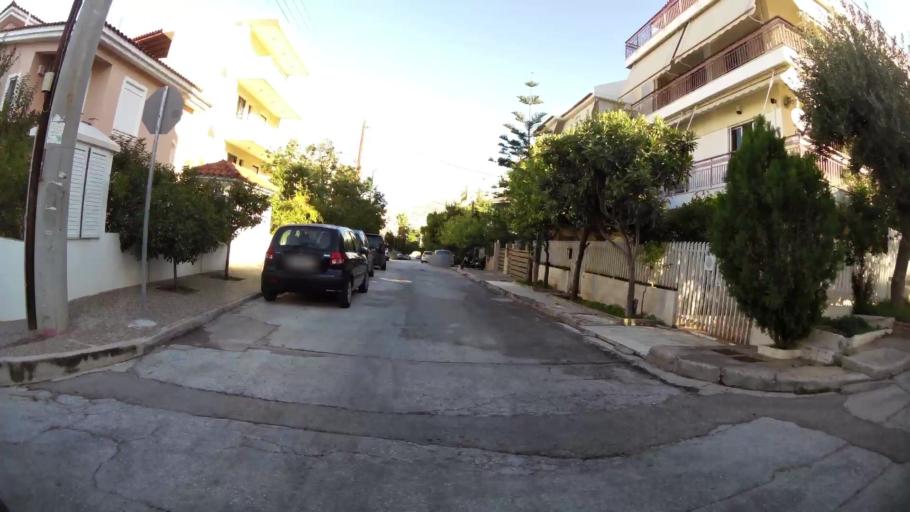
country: GR
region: Attica
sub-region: Nomarchia Athinas
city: Glyfada
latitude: 37.8764
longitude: 23.7703
